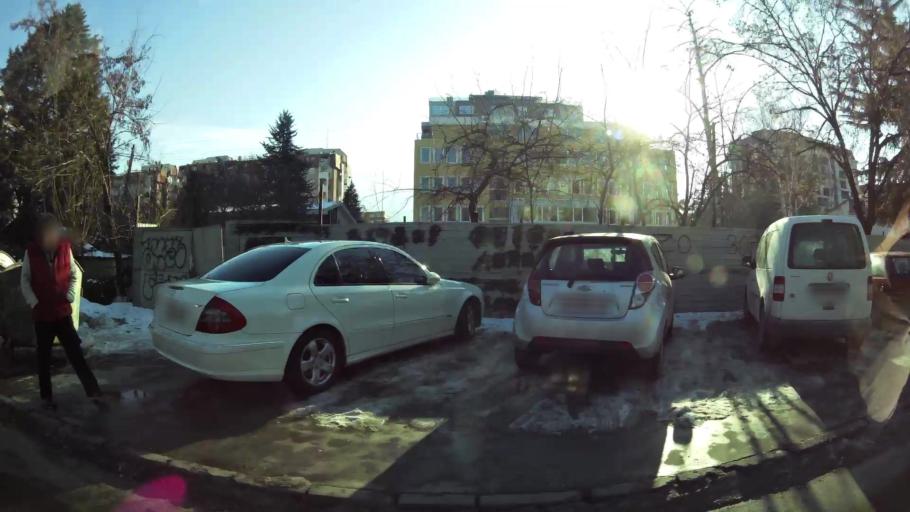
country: MK
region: Karpos
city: Skopje
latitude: 42.0044
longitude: 21.3969
